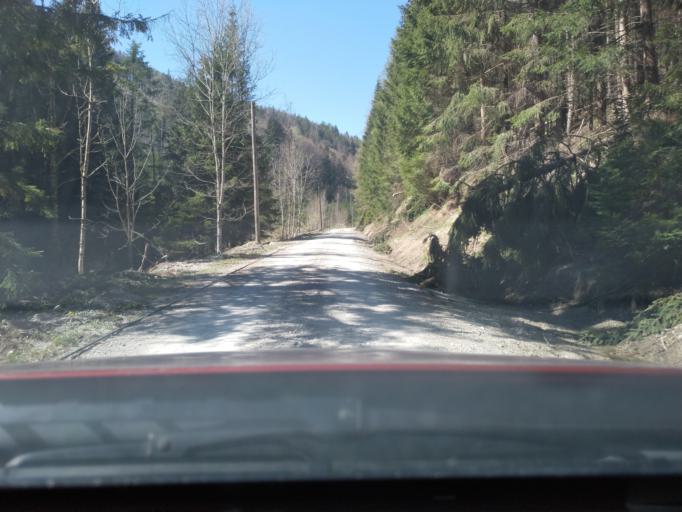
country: AT
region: Lower Austria
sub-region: Politischer Bezirk Neunkirchen
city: Puchberg am Schneeberg
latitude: 47.8144
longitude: 15.8450
